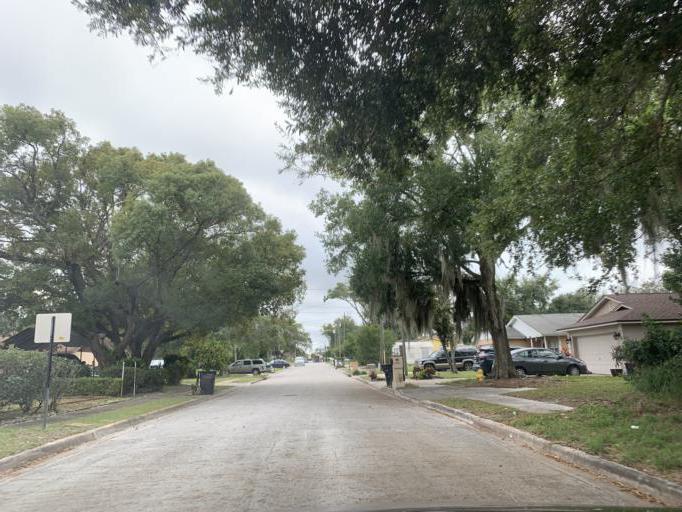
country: US
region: Florida
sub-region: Orange County
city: Eatonville
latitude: 28.6213
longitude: -81.3923
